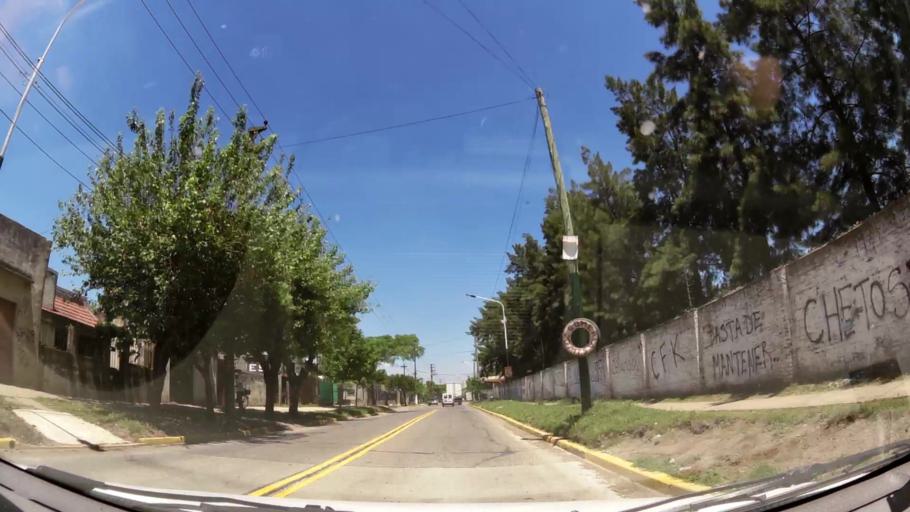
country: AR
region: Buenos Aires
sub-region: Partido de Merlo
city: Merlo
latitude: -34.6472
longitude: -58.7193
